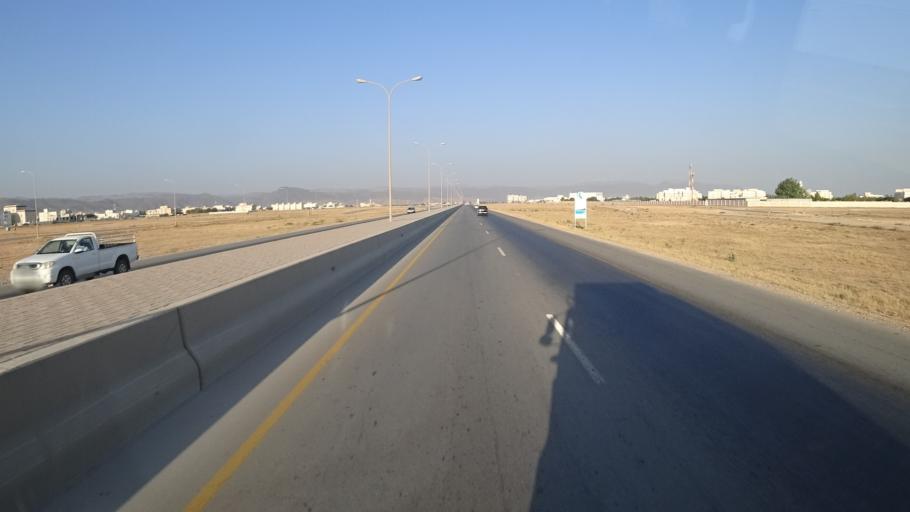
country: OM
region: Zufar
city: Salalah
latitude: 17.0891
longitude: 54.1359
